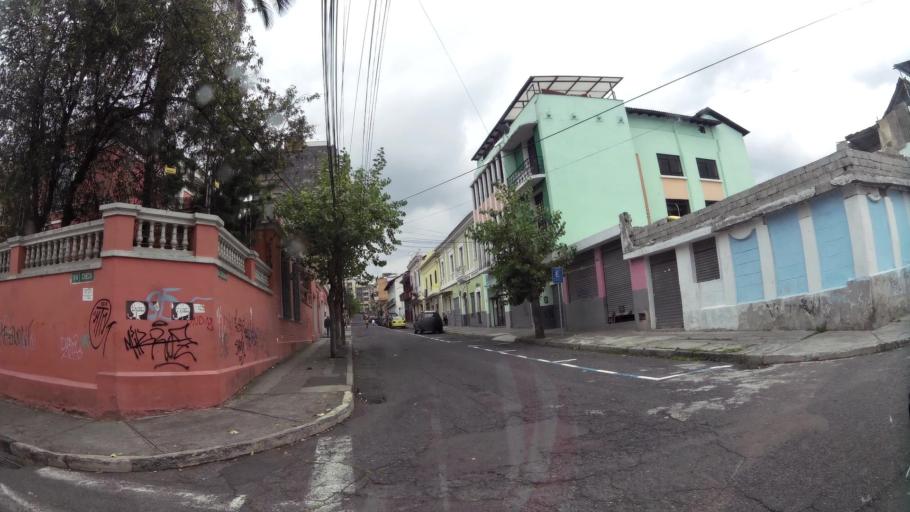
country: EC
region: Pichincha
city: Quito
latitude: -0.2117
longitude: -78.5036
